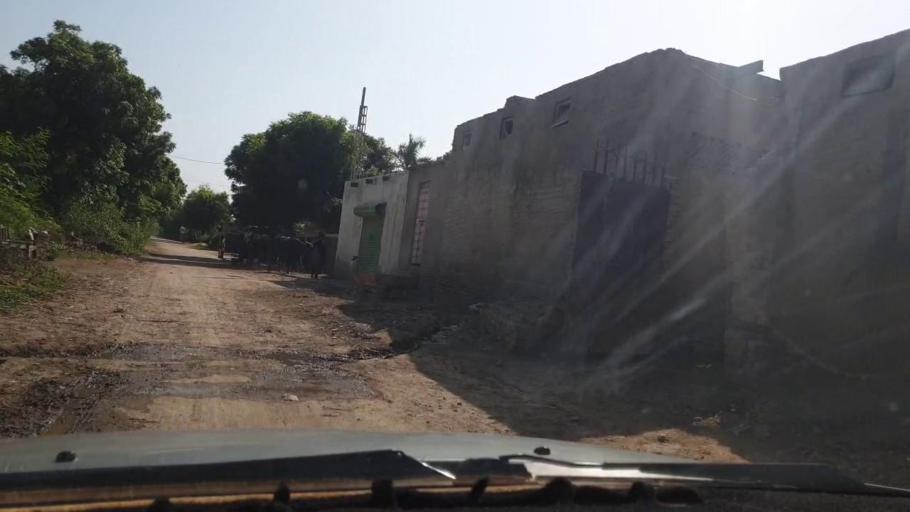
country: PK
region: Sindh
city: Chambar
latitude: 25.2414
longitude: 68.9060
